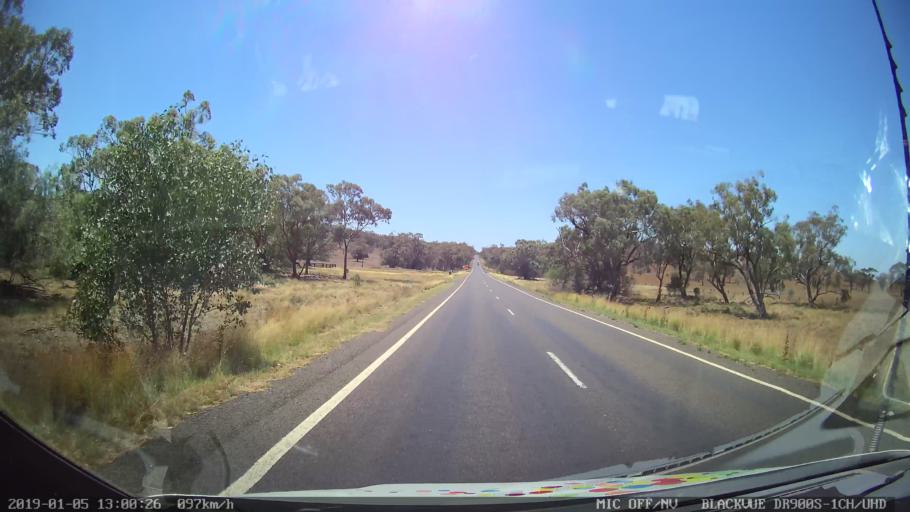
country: AU
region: New South Wales
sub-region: Narrabri
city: Boggabri
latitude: -31.1151
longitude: 149.7820
